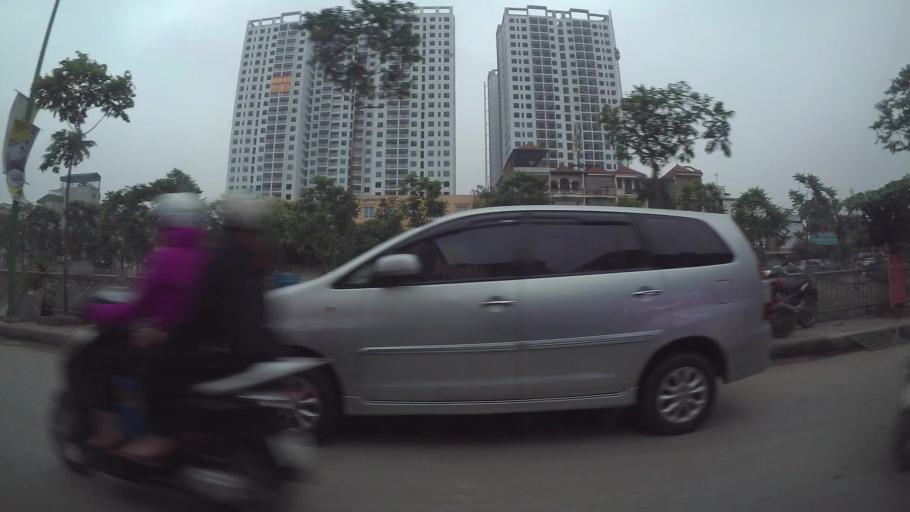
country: VN
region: Ha Noi
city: Hai BaTrung
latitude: 20.9844
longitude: 105.8344
